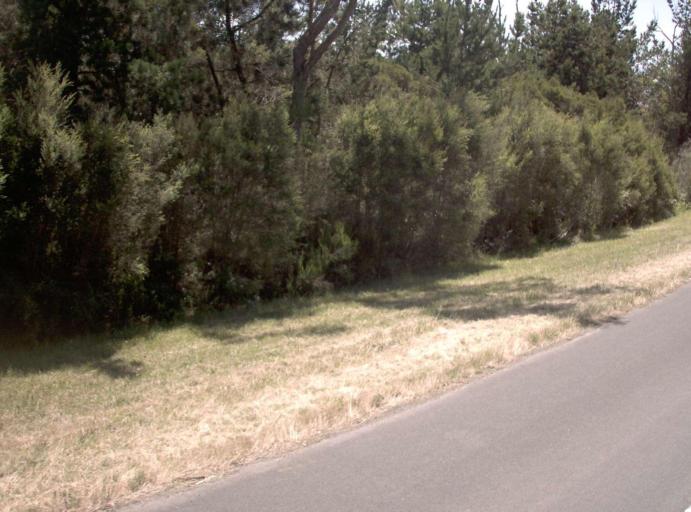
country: AU
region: Victoria
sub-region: Cardinia
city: Bunyip
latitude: -38.0772
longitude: 145.7080
